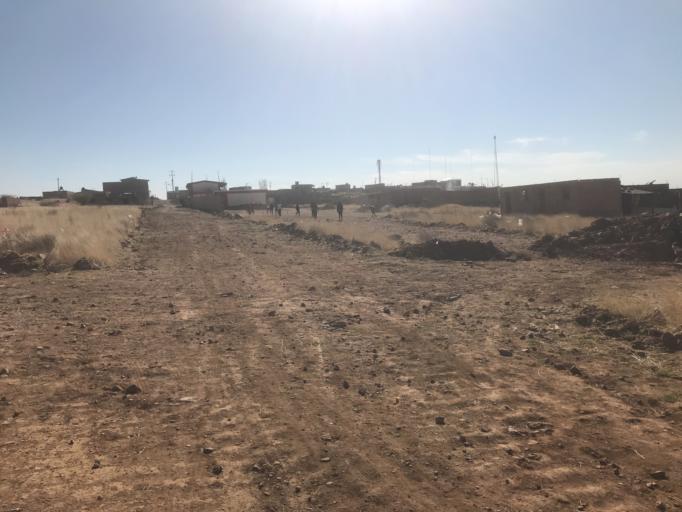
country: MX
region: Durango
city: Victoria de Durango
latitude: 24.0445
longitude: -104.7037
